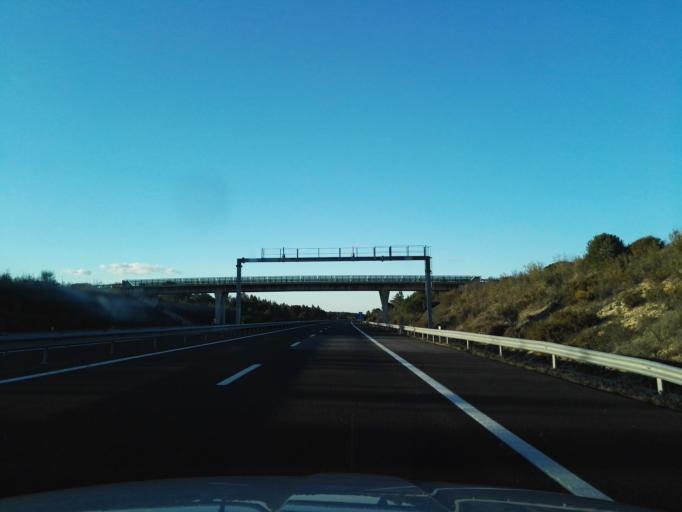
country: PT
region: Santarem
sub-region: Benavente
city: Poceirao
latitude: 38.8133
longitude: -8.7075
